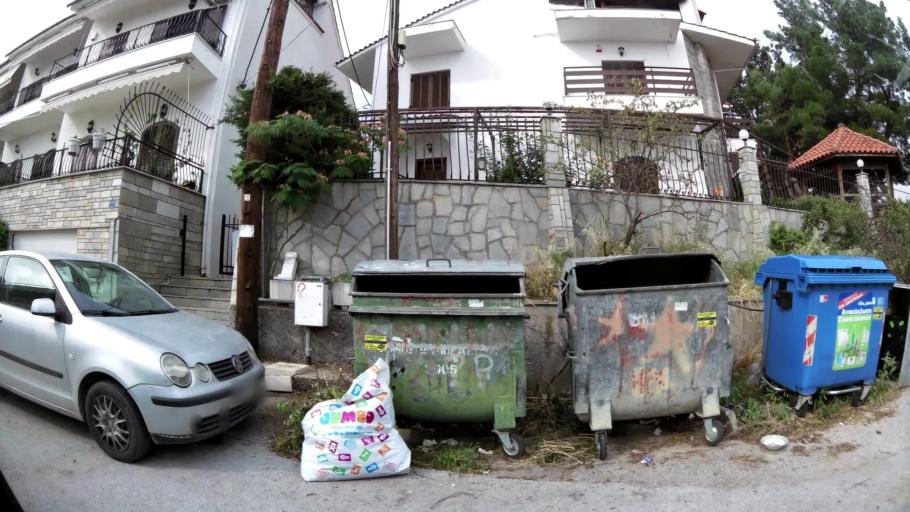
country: GR
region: Central Macedonia
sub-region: Nomos Thessalonikis
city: Oraiokastro
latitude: 40.7320
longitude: 22.9239
